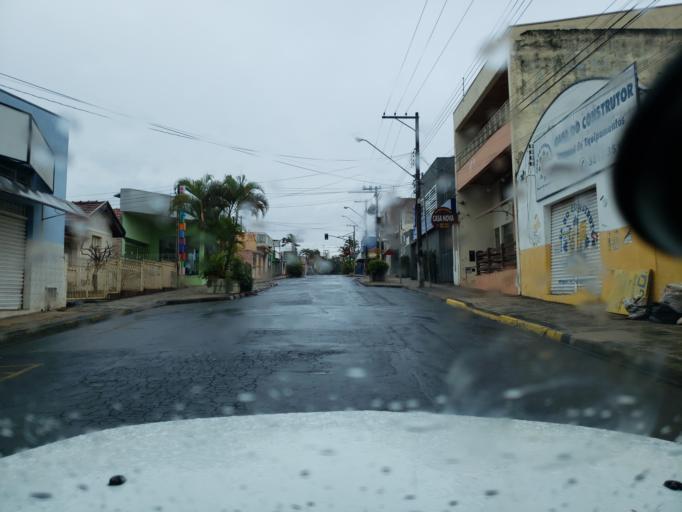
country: BR
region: Sao Paulo
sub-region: Moji-Guacu
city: Mogi-Gaucu
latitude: -22.3632
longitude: -46.9440
